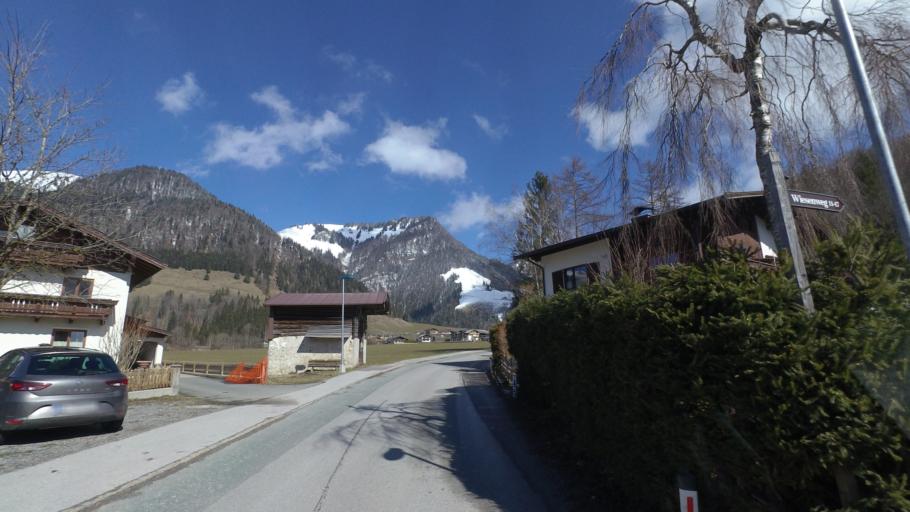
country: AT
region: Tyrol
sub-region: Politischer Bezirk Kufstein
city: Walchsee
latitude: 47.6569
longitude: 12.3188
